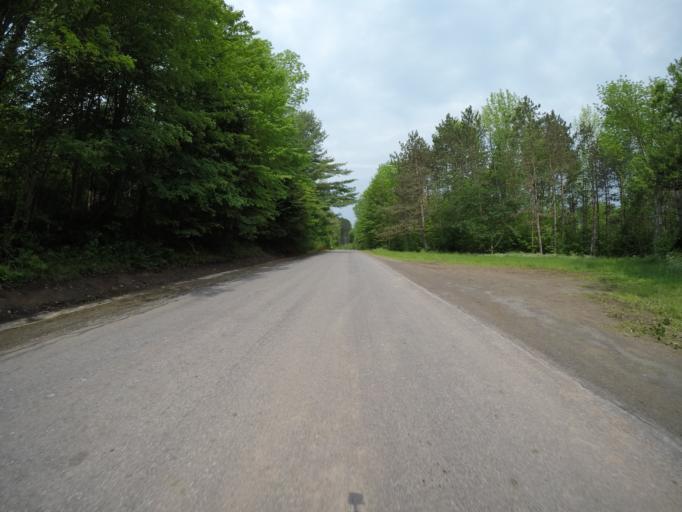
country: US
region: New York
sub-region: Sullivan County
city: Livingston Manor
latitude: 42.0822
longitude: -74.7926
